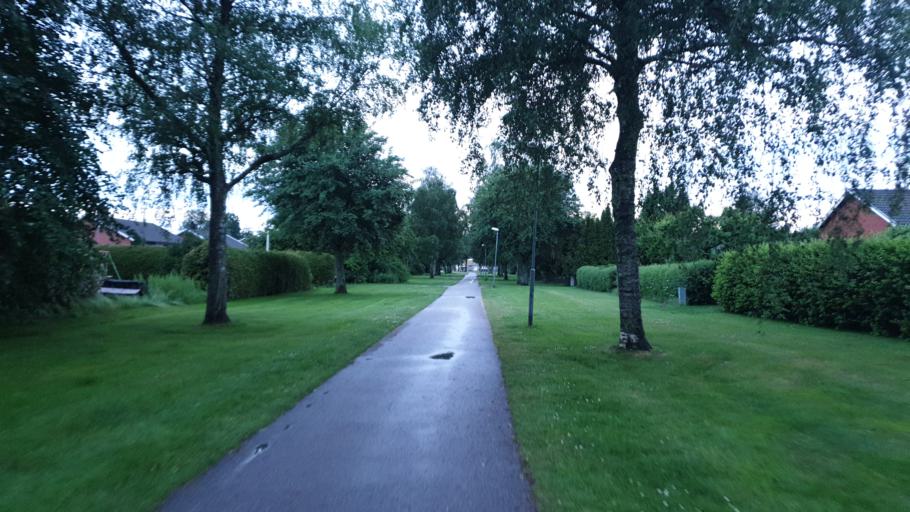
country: SE
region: Kronoberg
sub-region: Ljungby Kommun
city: Ljungby
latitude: 56.8324
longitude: 13.9610
